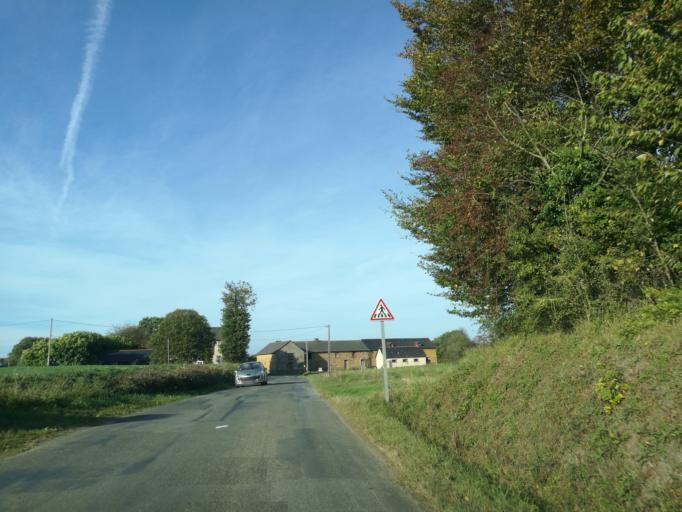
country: FR
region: Brittany
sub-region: Departement d'Ille-et-Vilaine
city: Montauban-de-Bretagne
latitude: 48.2080
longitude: -1.9934
